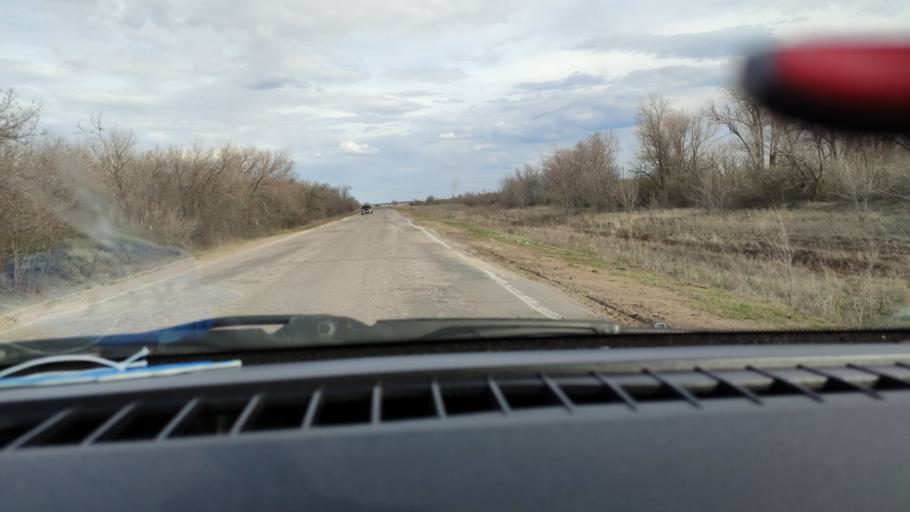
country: RU
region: Saratov
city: Rovnoye
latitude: 51.0657
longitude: 46.0072
